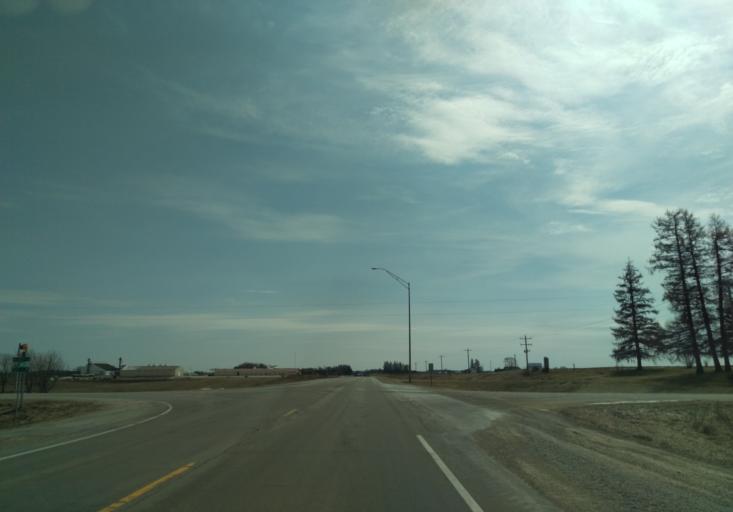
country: US
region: Iowa
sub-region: Winneshiek County
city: Decorah
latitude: 43.4437
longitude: -91.8620
